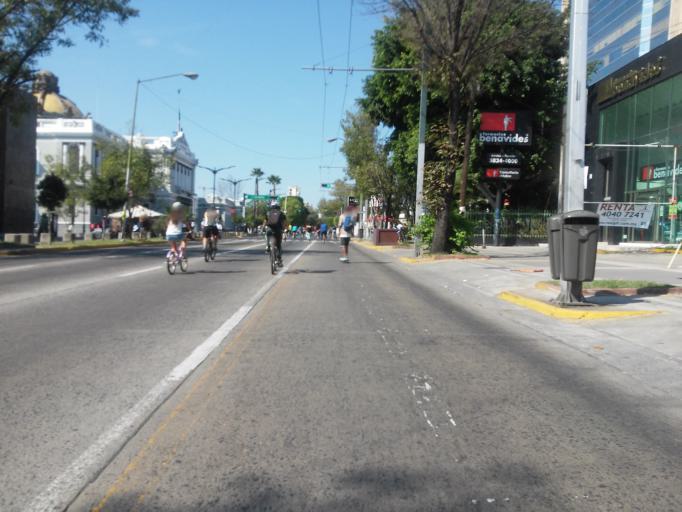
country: MX
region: Jalisco
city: Guadalajara
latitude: 20.6749
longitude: -103.3579
